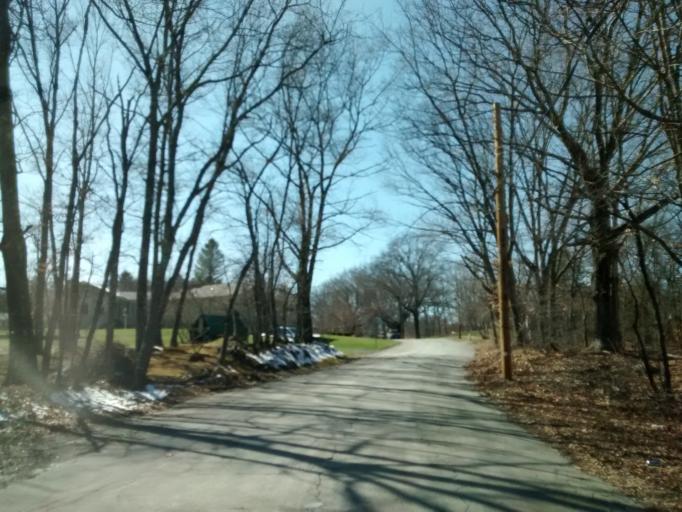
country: US
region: Massachusetts
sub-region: Worcester County
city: Millbury
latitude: 42.1871
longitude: -71.7471
